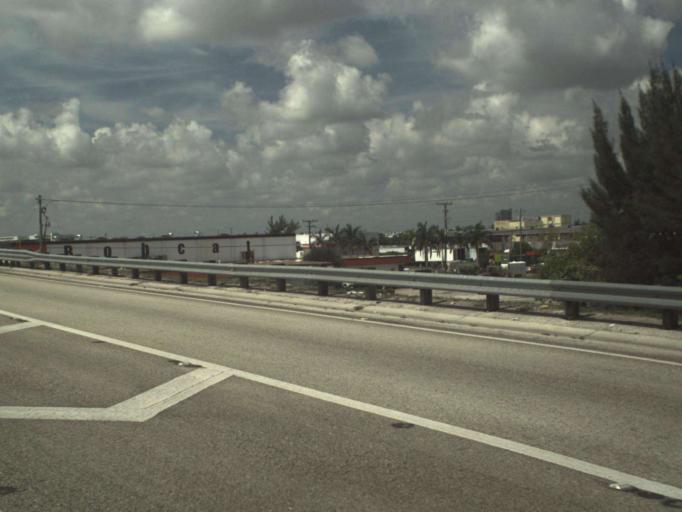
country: US
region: Florida
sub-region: Broward County
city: Pompano Beach
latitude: 26.2350
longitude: -80.1367
